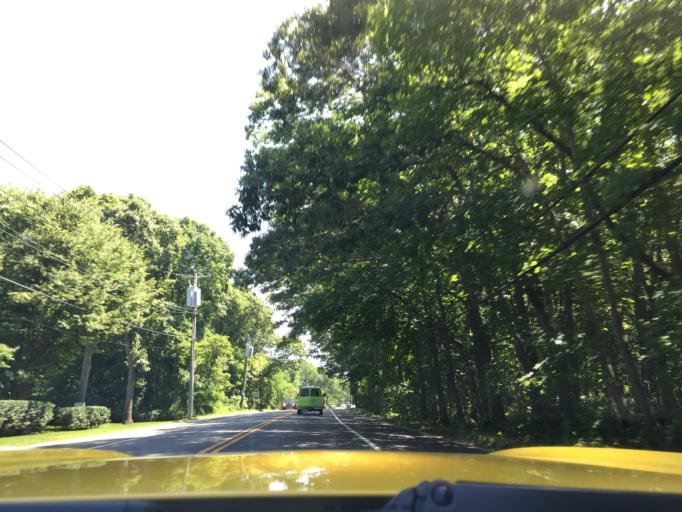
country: US
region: New York
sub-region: Suffolk County
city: Bridgehampton
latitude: 40.9456
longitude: -72.2586
